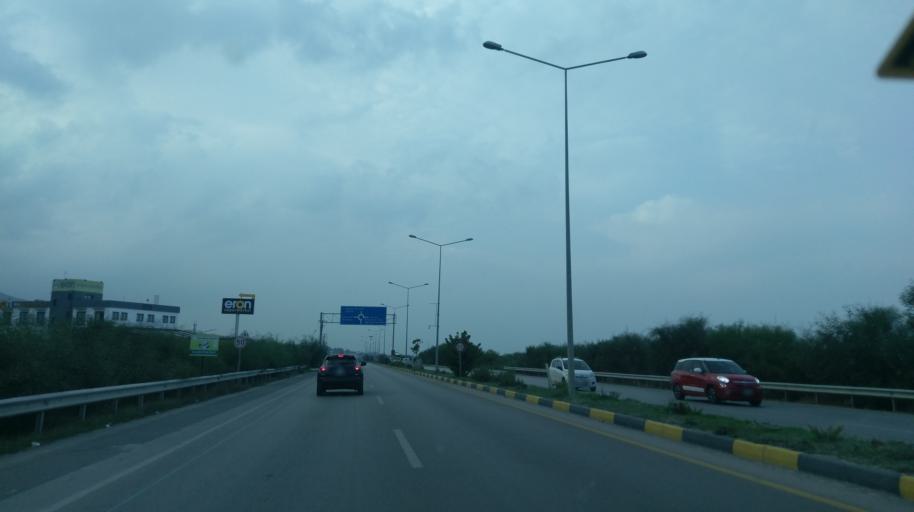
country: CY
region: Keryneia
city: Kyrenia
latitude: 35.3300
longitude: 33.2785
